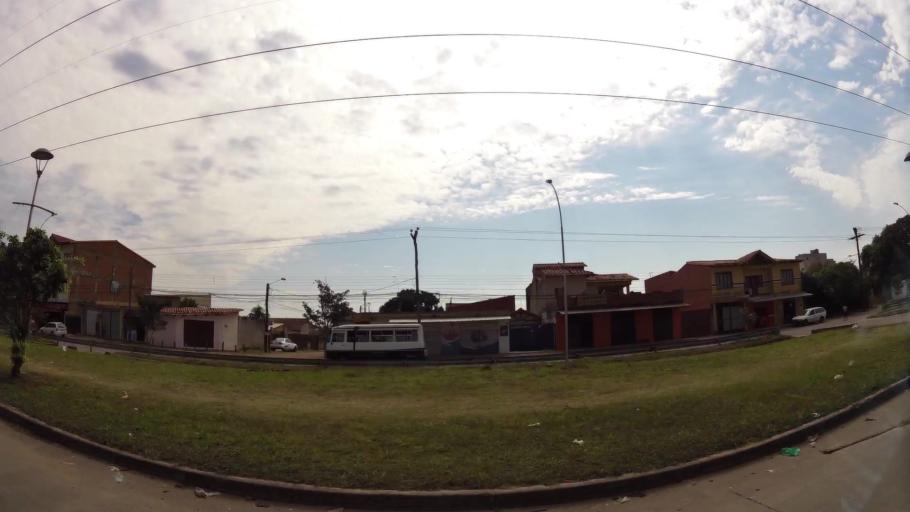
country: BO
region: Santa Cruz
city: Santa Cruz de la Sierra
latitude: -17.7467
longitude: -63.1552
